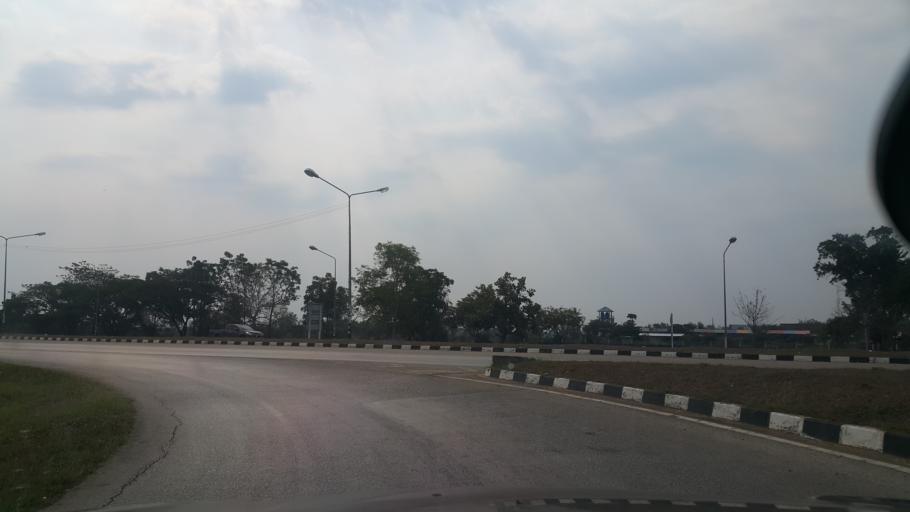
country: TH
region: Sukhothai
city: Sukhothai
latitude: 17.0643
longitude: 99.8767
